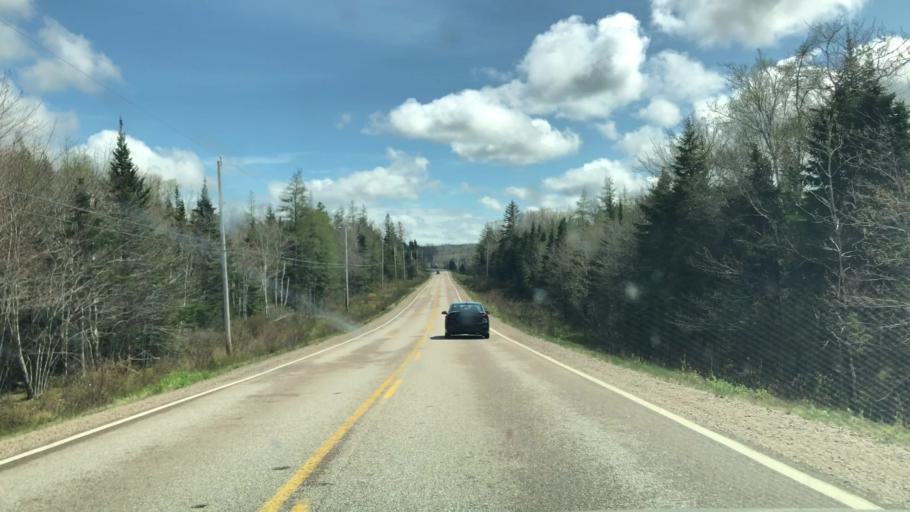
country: CA
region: Nova Scotia
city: Antigonish
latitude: 45.2062
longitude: -62.0037
